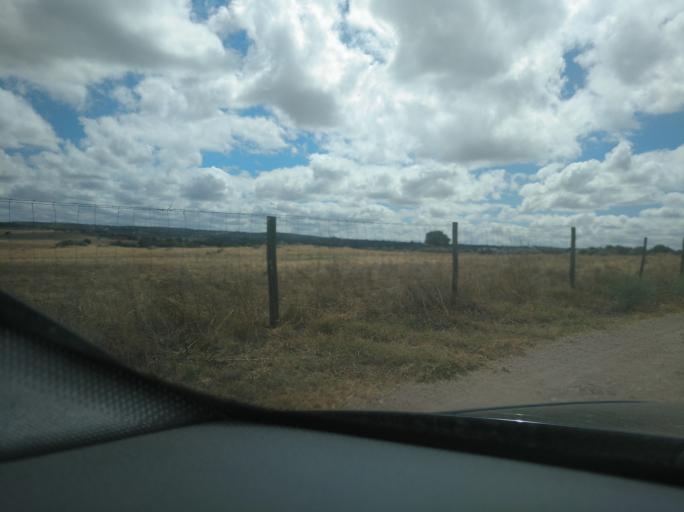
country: PT
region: Portalegre
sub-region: Arronches
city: Arronches
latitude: 39.0151
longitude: -7.2368
